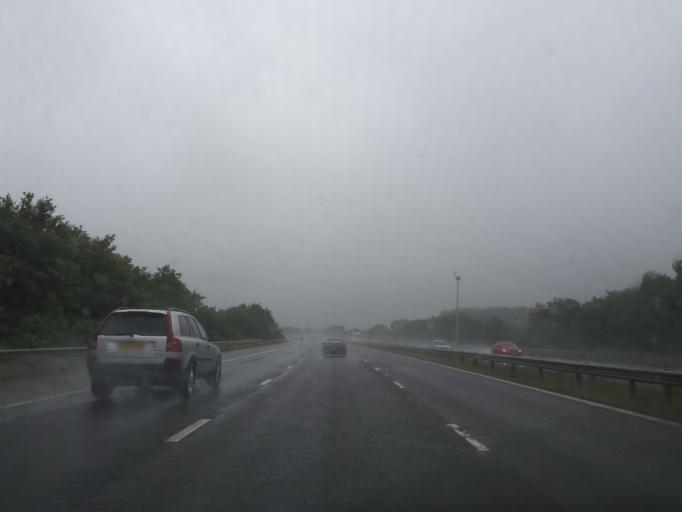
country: GB
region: England
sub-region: Leicestershire
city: Markfield
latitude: 52.6975
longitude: -1.2925
